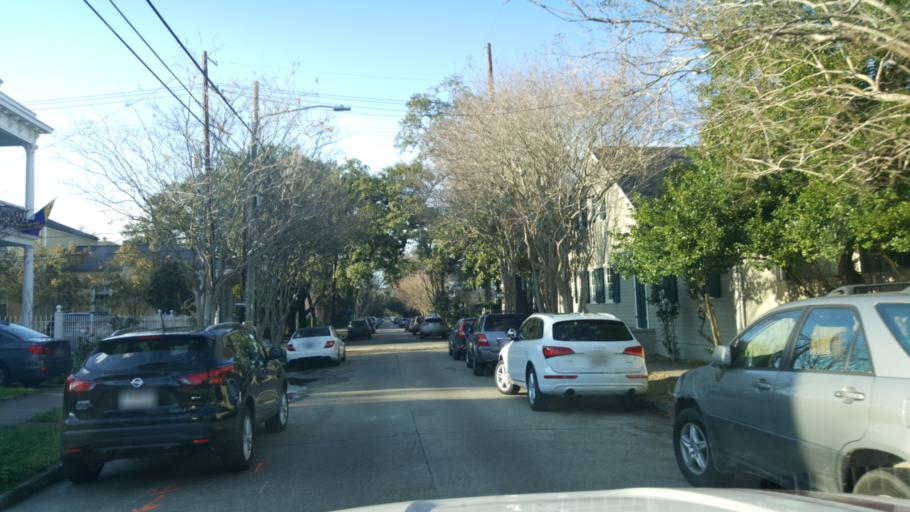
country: US
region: Louisiana
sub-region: Orleans Parish
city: New Orleans
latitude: 29.9307
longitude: -90.0762
